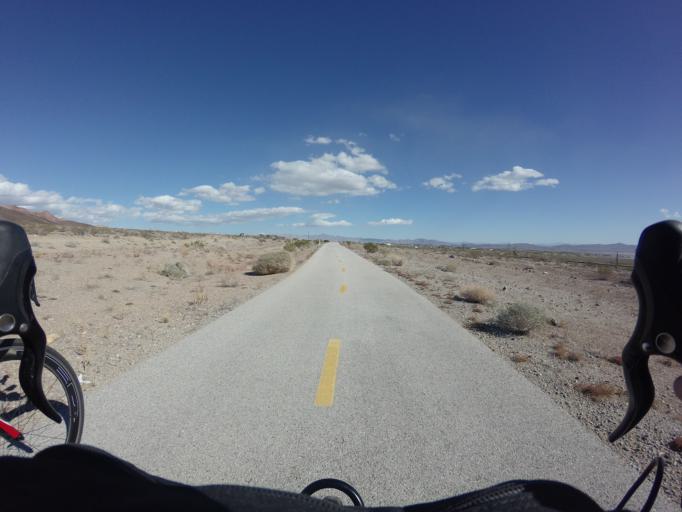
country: US
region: Nevada
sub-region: Clark County
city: Boulder City
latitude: 35.9680
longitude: -114.8795
